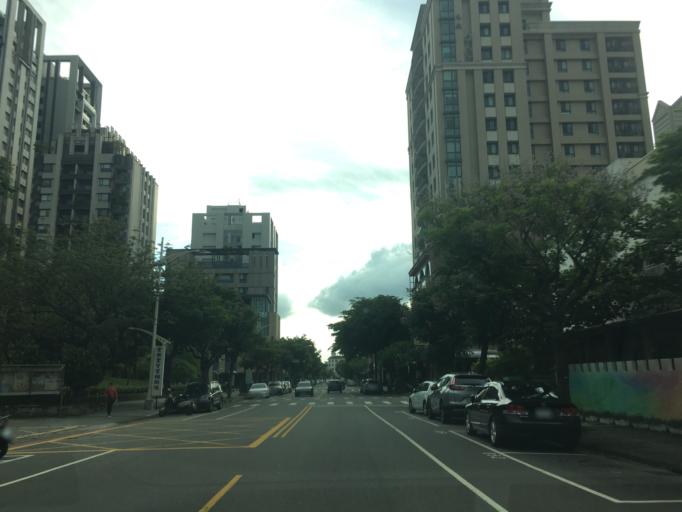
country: TW
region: Taiwan
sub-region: Taichung City
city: Taichung
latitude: 24.1321
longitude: 120.6425
